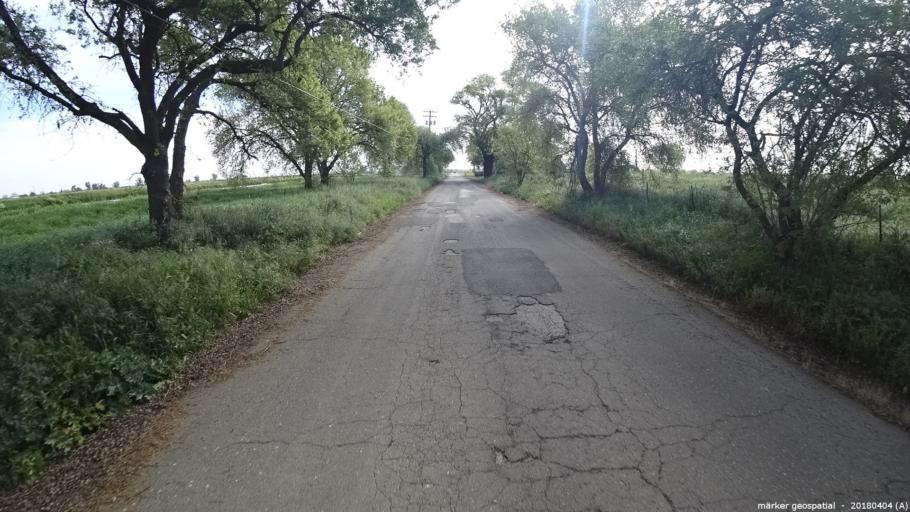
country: US
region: California
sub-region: Sacramento County
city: Herald
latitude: 38.2558
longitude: -121.2241
